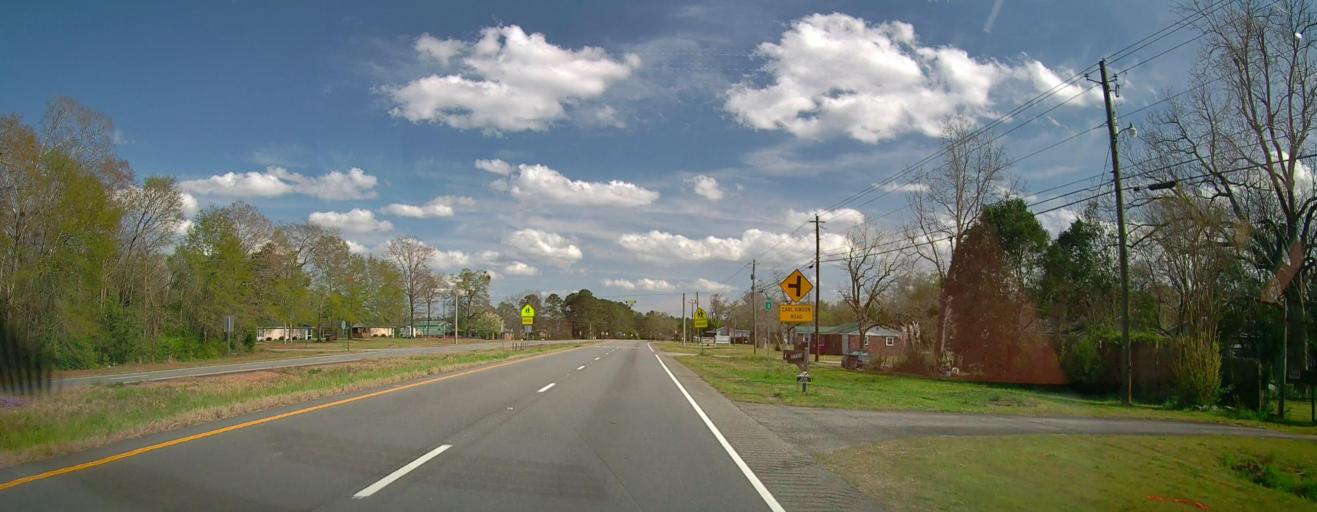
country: US
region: Georgia
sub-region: Baldwin County
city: Hardwick
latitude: 33.0210
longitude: -83.2307
